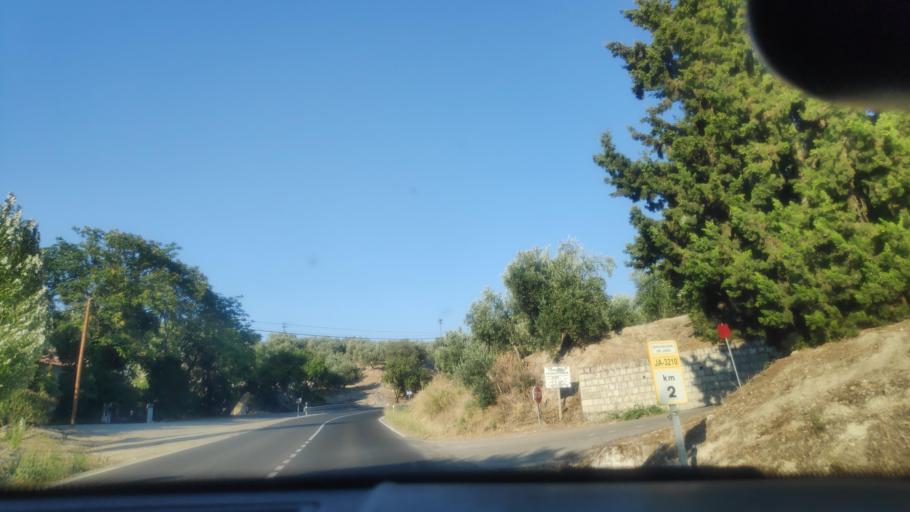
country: ES
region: Andalusia
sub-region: Provincia de Jaen
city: Jaen
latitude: 37.7478
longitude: -3.7883
